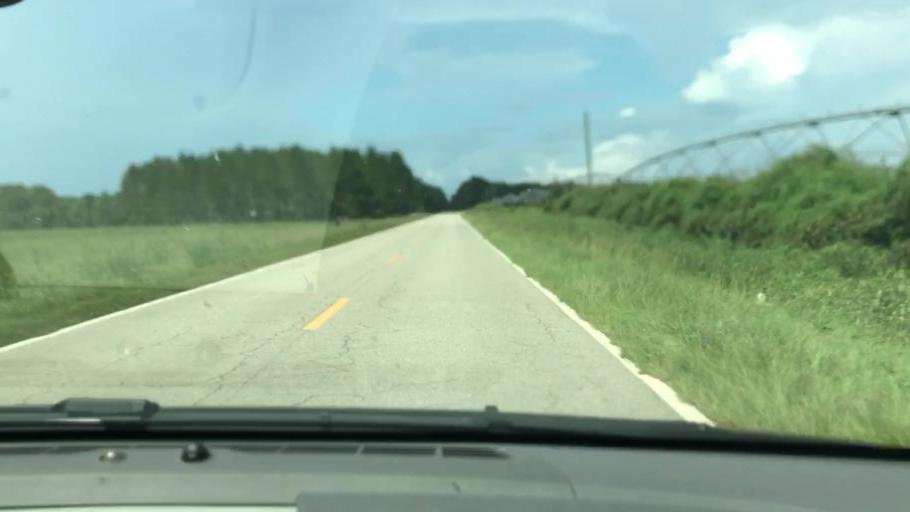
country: US
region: Georgia
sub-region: Seminole County
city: Donalsonville
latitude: 31.1416
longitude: -84.9951
